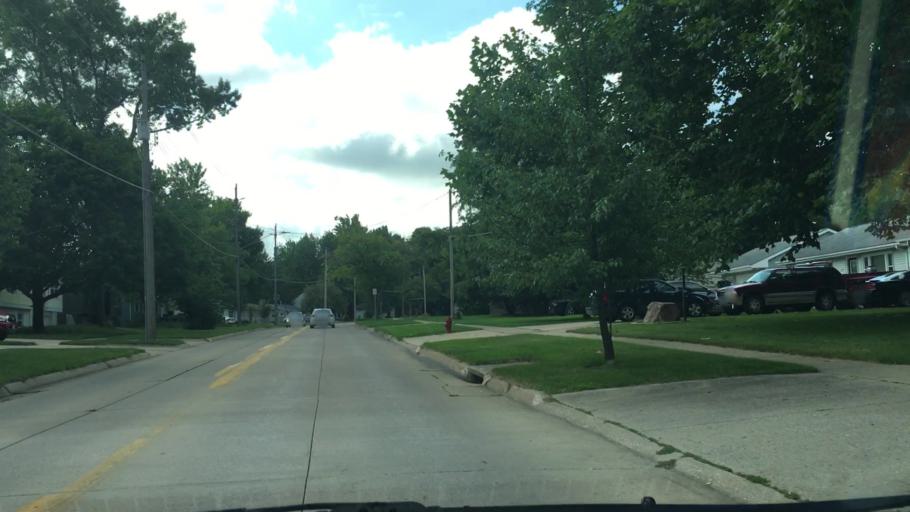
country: US
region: Iowa
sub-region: Johnson County
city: Iowa City
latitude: 41.6836
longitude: -91.5223
